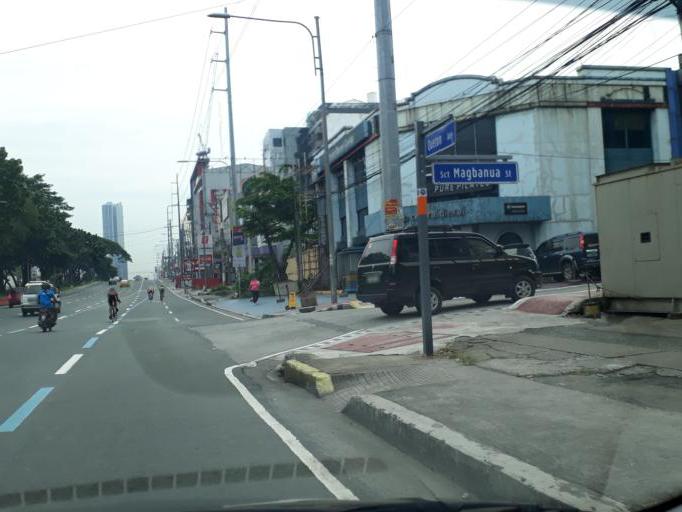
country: PH
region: Calabarzon
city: Del Monte
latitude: 14.6347
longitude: 121.0224
